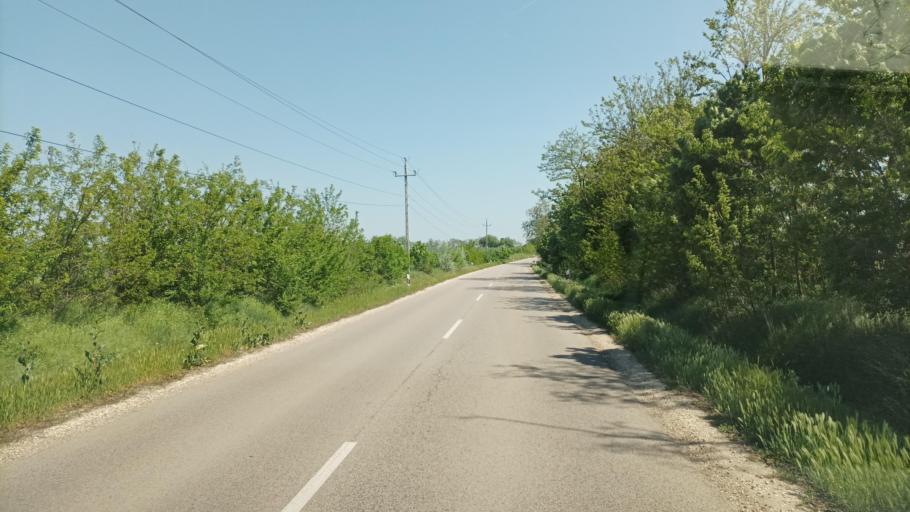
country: HU
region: Pest
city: Uri
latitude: 47.4314
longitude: 19.5302
